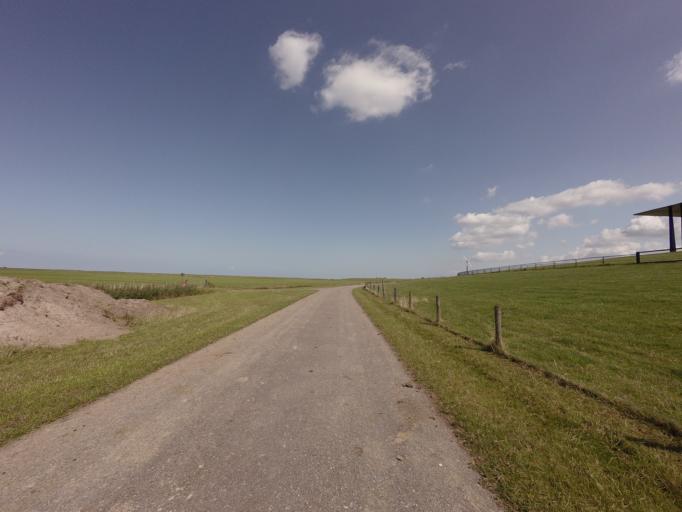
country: NL
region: Friesland
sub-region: Gemeente Ferwerderadiel
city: Hallum
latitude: 53.3321
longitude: 5.7760
